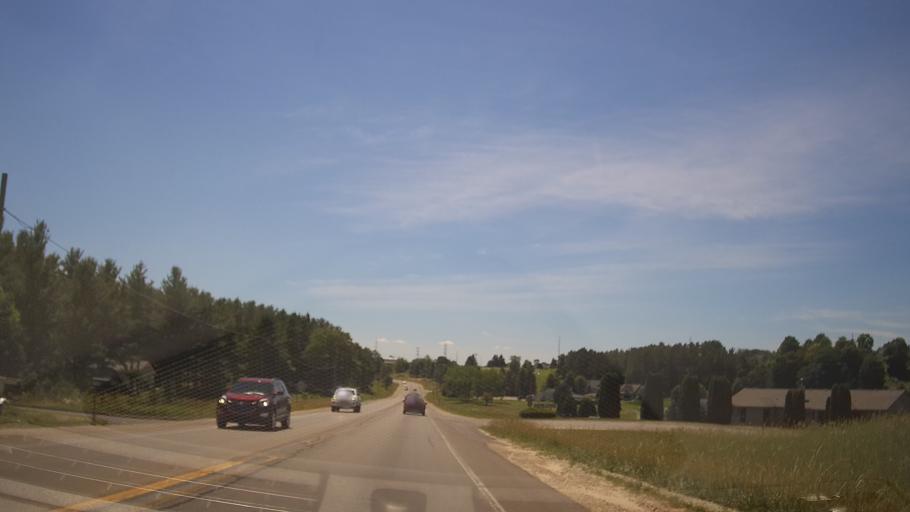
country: US
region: Michigan
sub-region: Grand Traverse County
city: Traverse City
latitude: 44.7243
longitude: -85.6786
